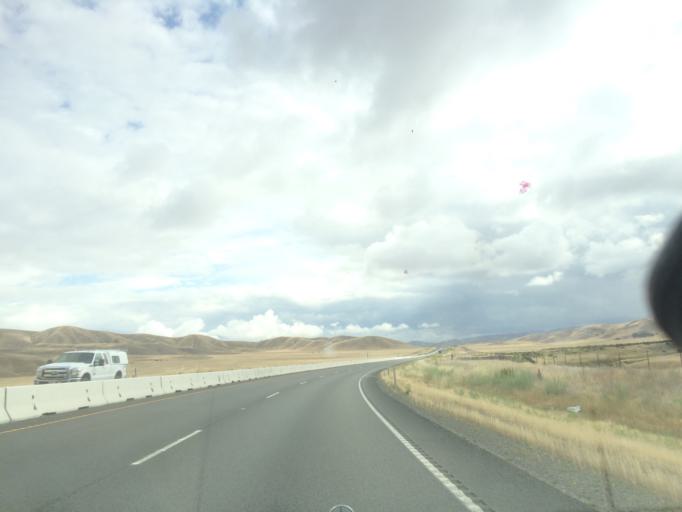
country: US
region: California
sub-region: San Luis Obispo County
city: Shandon
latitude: 35.7028
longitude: -120.3224
